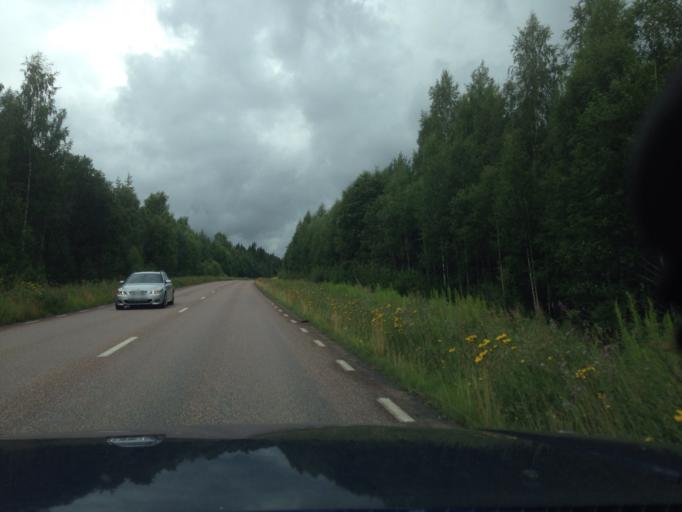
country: SE
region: Dalarna
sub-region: Ludvika Kommun
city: Ludvika
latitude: 60.1413
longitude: 15.1273
